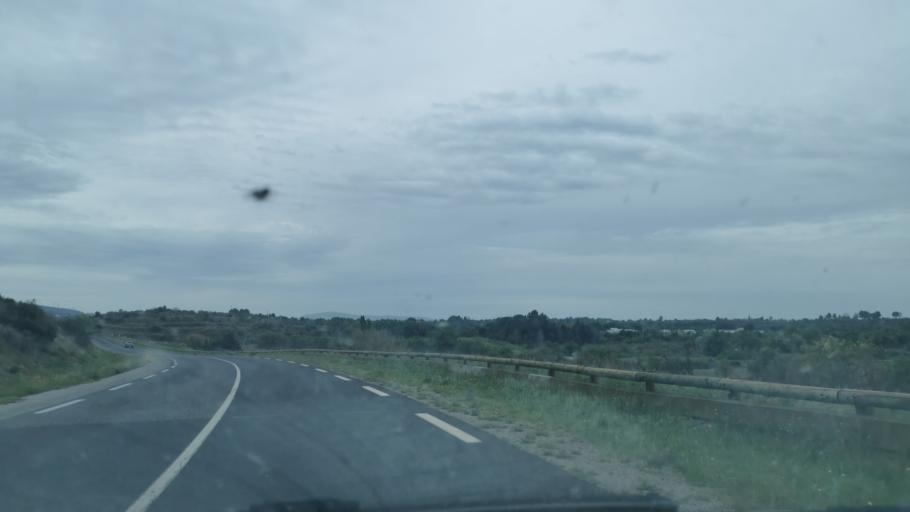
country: FR
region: Languedoc-Roussillon
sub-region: Departement de l'Herault
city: Poussan
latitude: 43.5024
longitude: 3.6835
